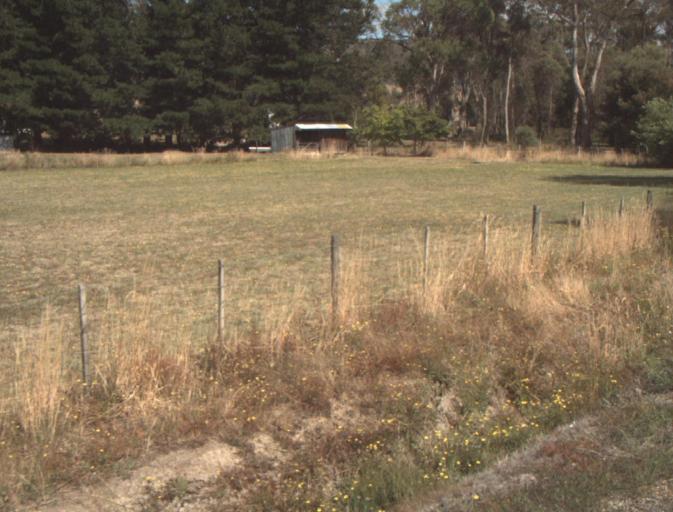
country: AU
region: Tasmania
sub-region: Launceston
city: Mayfield
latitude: -41.2566
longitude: 147.1521
